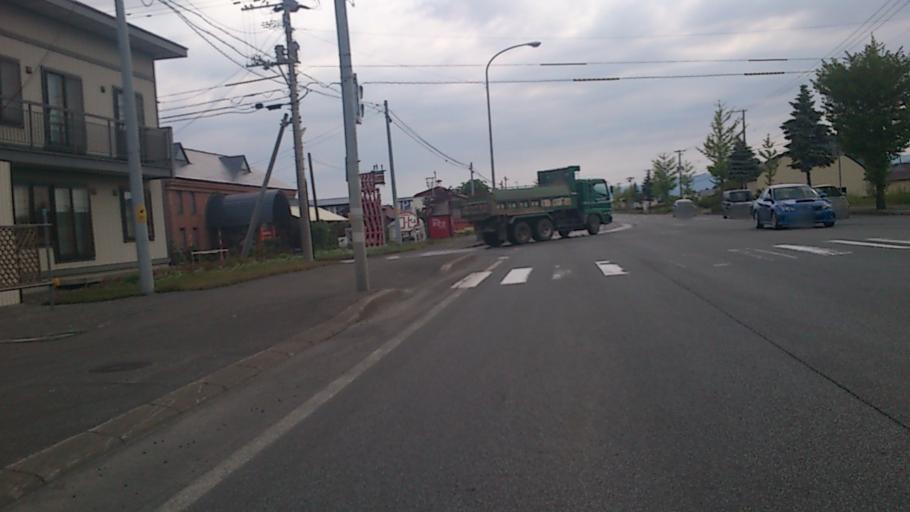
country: JP
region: Hokkaido
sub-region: Asahikawa-shi
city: Asahikawa
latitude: 43.8354
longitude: 142.4737
